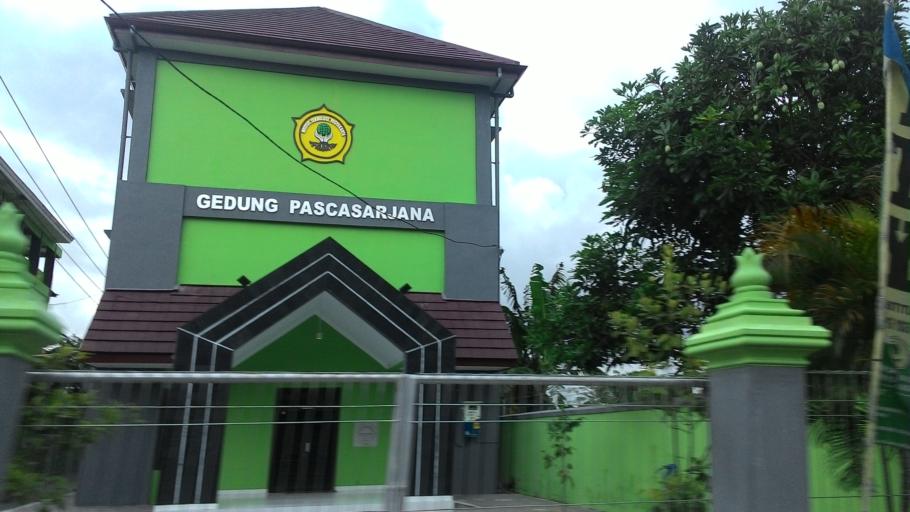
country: ID
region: Daerah Istimewa Yogyakarta
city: Yogyakarta
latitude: -7.7994
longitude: 110.4023
